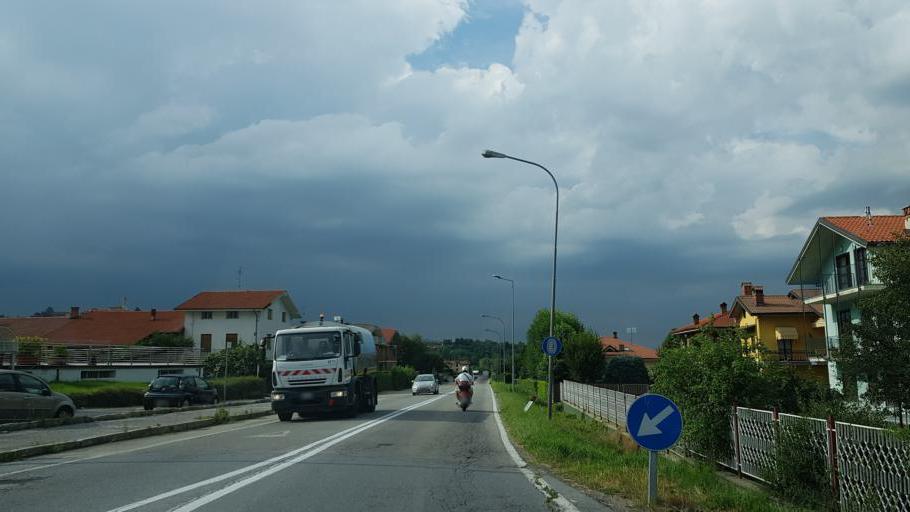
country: IT
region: Piedmont
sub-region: Provincia di Cuneo
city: Vignolo
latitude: 44.3610
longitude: 7.4762
